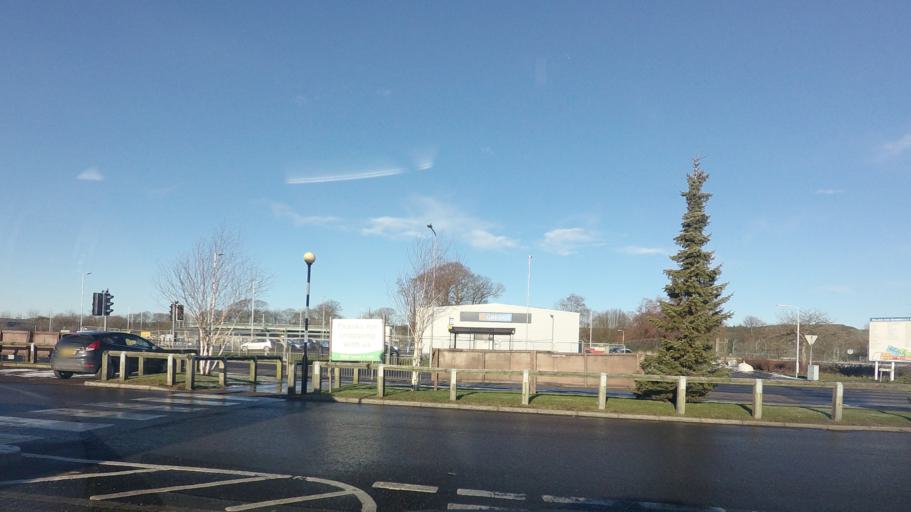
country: GB
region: Scotland
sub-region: Fife
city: Crossgates
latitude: 56.0413
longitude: -3.3591
